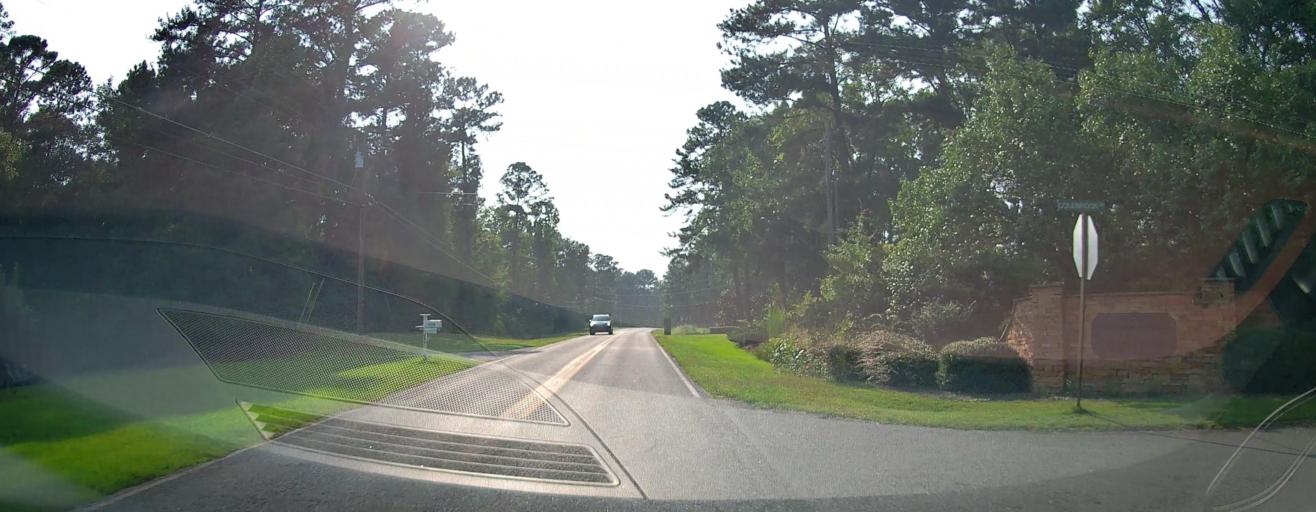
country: US
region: Georgia
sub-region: Bibb County
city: Macon
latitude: 32.9568
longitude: -83.7371
